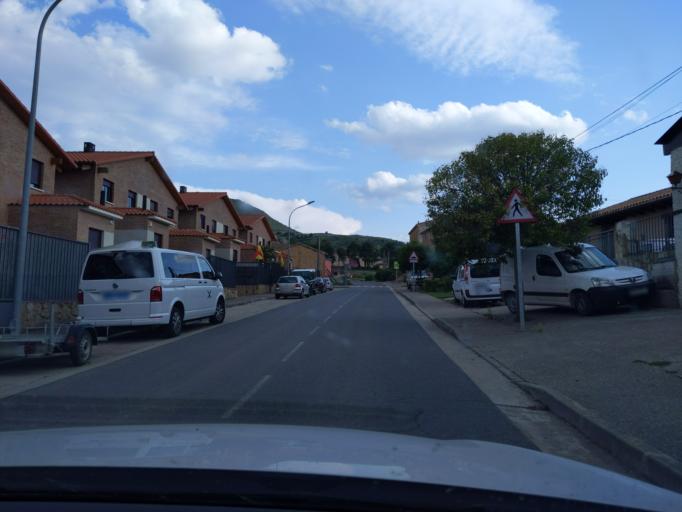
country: ES
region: La Rioja
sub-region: Provincia de La Rioja
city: Clavijo
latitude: 42.3709
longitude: -2.4228
